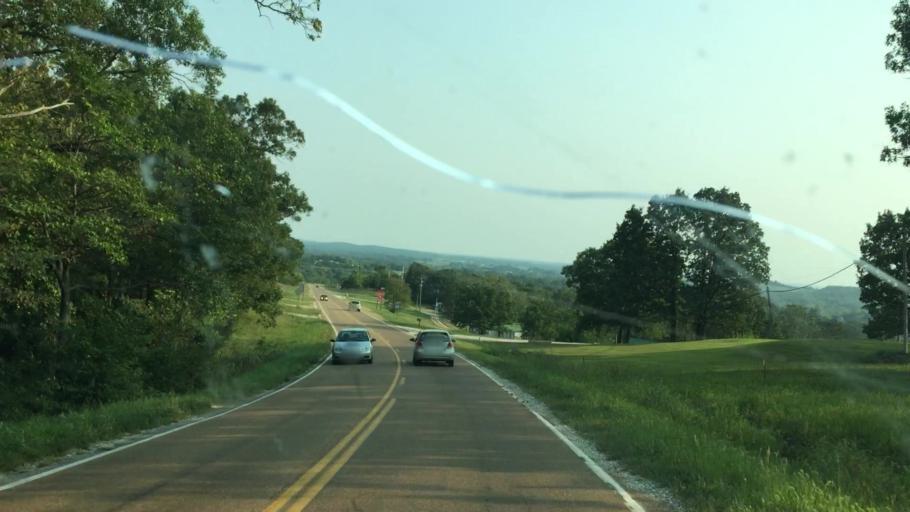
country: US
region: Missouri
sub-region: Pulaski County
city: Richland
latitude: 37.8447
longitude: -92.4110
